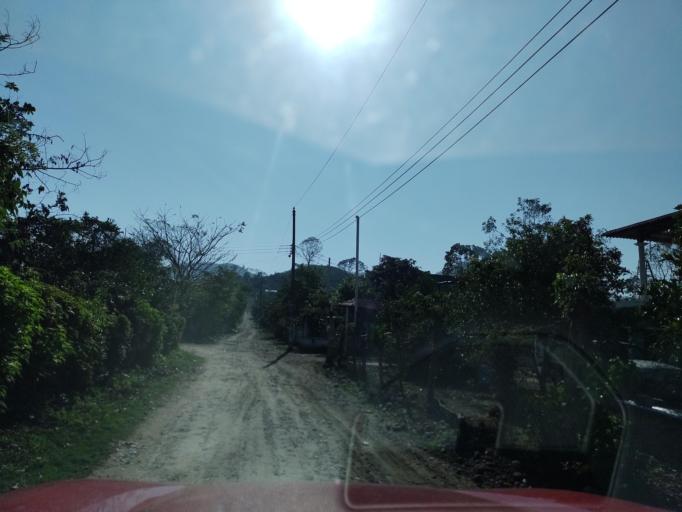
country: MX
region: Veracruz
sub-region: Papantla
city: Polutla
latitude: 20.5160
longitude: -97.2461
